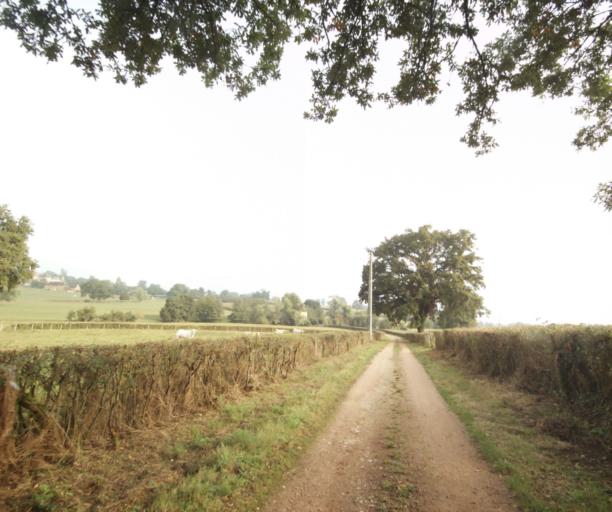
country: FR
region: Bourgogne
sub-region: Departement de Saone-et-Loire
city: Charolles
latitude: 46.4483
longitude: 4.2903
